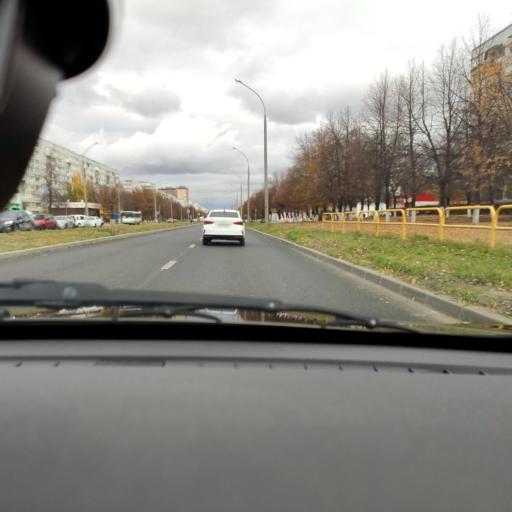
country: RU
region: Samara
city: Tol'yatti
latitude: 53.5339
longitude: 49.3288
